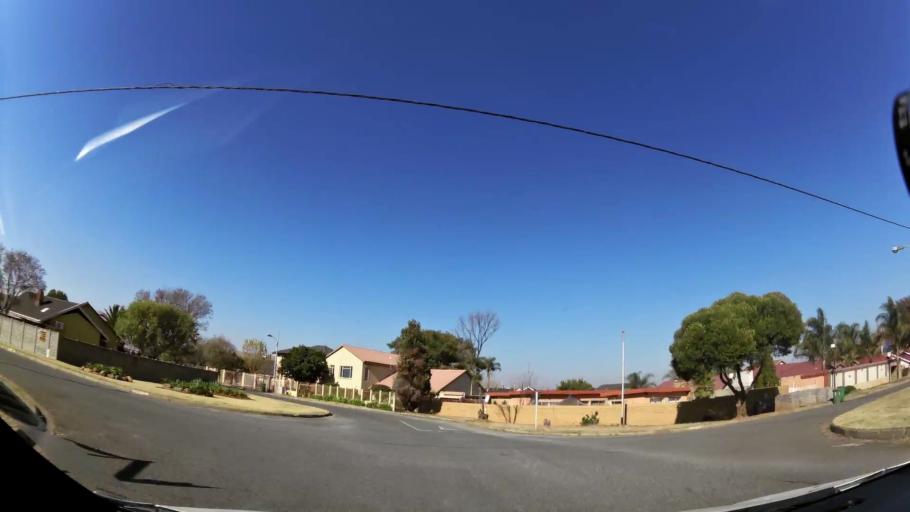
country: ZA
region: Gauteng
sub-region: City of Johannesburg Metropolitan Municipality
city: Johannesburg
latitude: -26.2548
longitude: 28.1012
